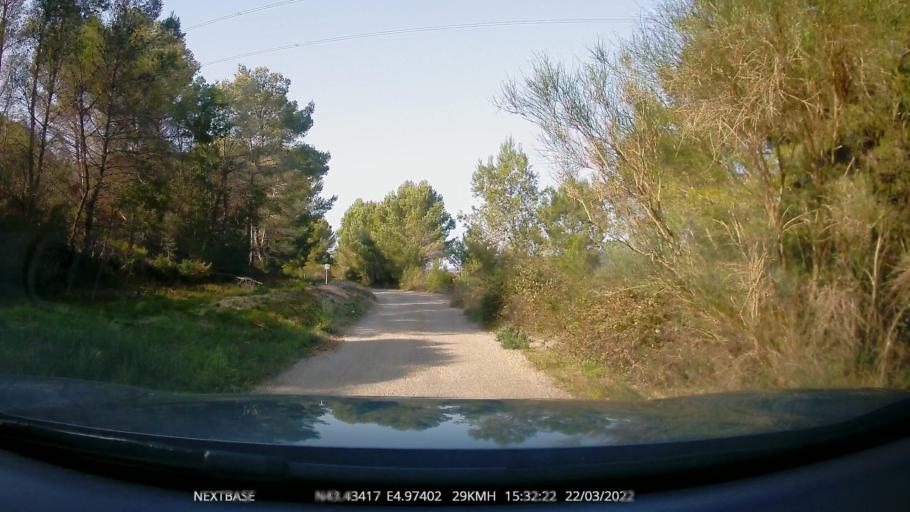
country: FR
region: Provence-Alpes-Cote d'Azur
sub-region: Departement des Bouches-du-Rhone
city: Port-de-Bouc
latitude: 43.4342
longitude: 4.9740
